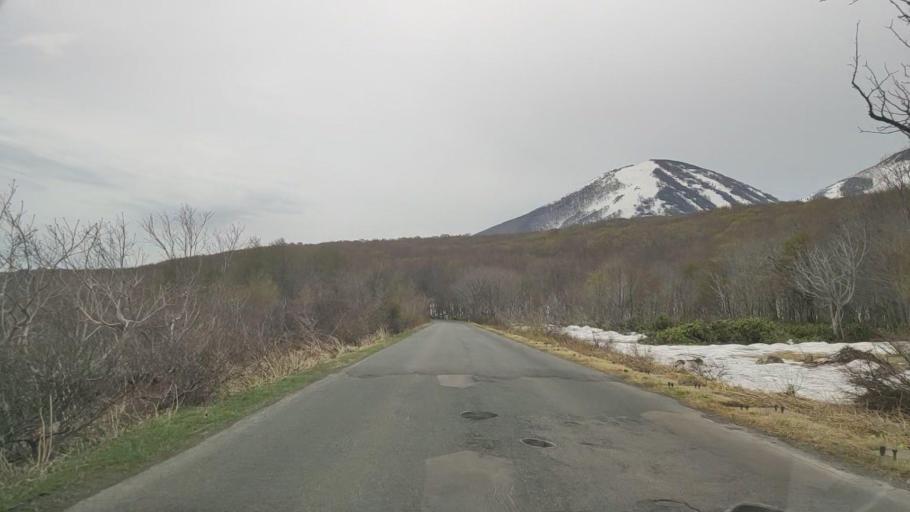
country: JP
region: Aomori
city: Aomori Shi
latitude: 40.6855
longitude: 140.9259
